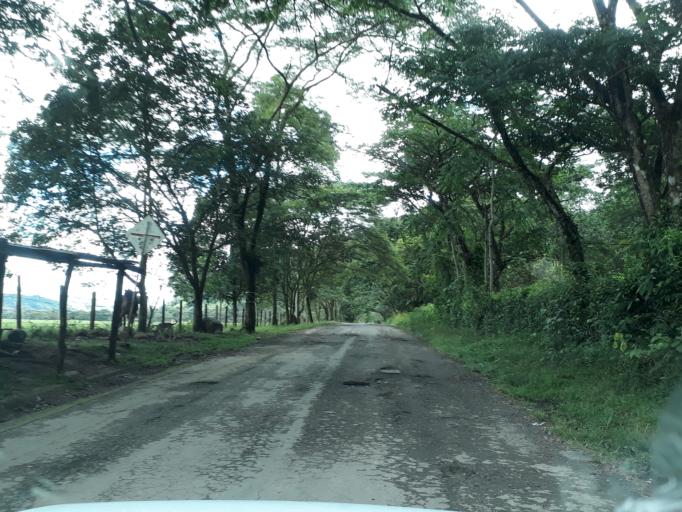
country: CO
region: Cundinamarca
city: Medina
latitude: 4.5621
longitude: -73.3635
